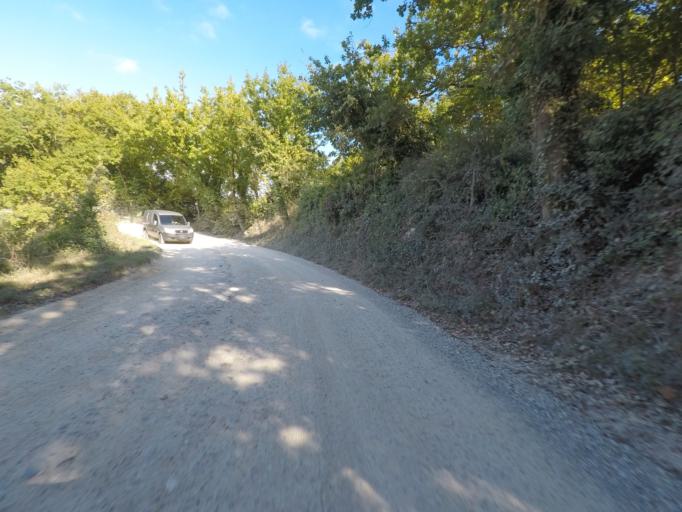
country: IT
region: Tuscany
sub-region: Provincia di Siena
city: Castellina in Chianti
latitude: 43.4398
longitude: 11.3102
